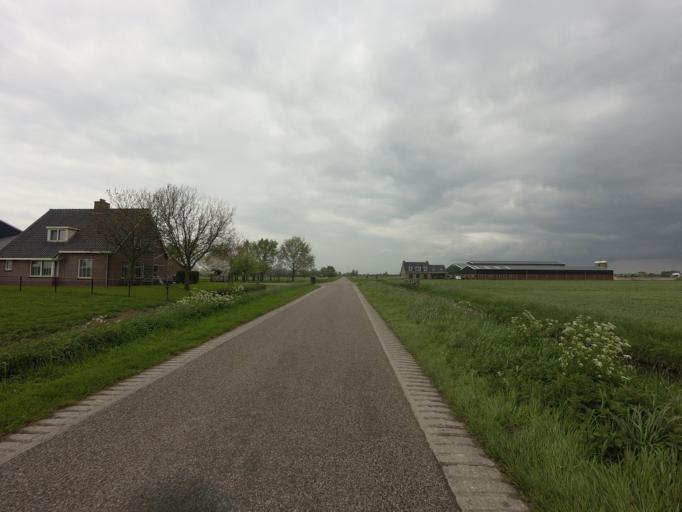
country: NL
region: Utrecht
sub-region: Gemeente Montfoort
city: Montfoort
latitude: 52.0362
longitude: 4.9983
